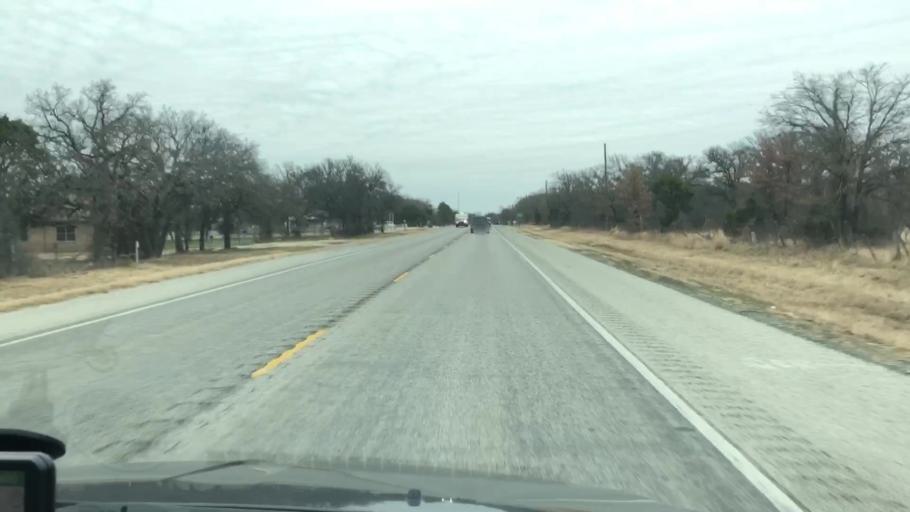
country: US
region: Texas
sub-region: Palo Pinto County
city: Mineral Wells
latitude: 32.8964
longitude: -98.0854
